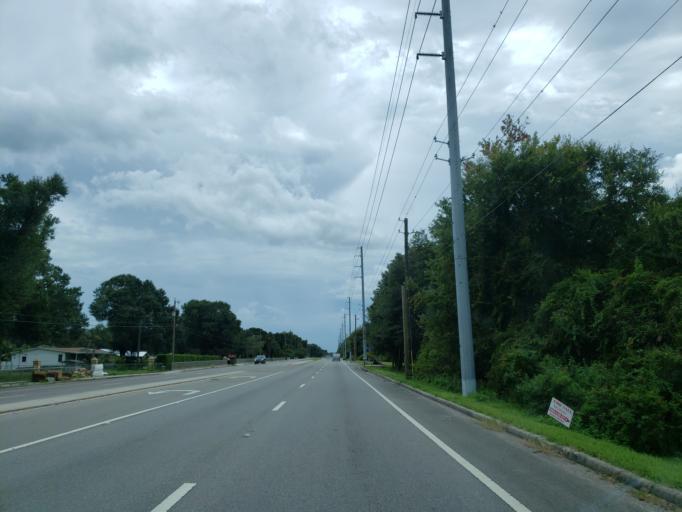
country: US
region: Florida
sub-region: Polk County
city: Willow Oak
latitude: 27.9449
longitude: -82.0554
